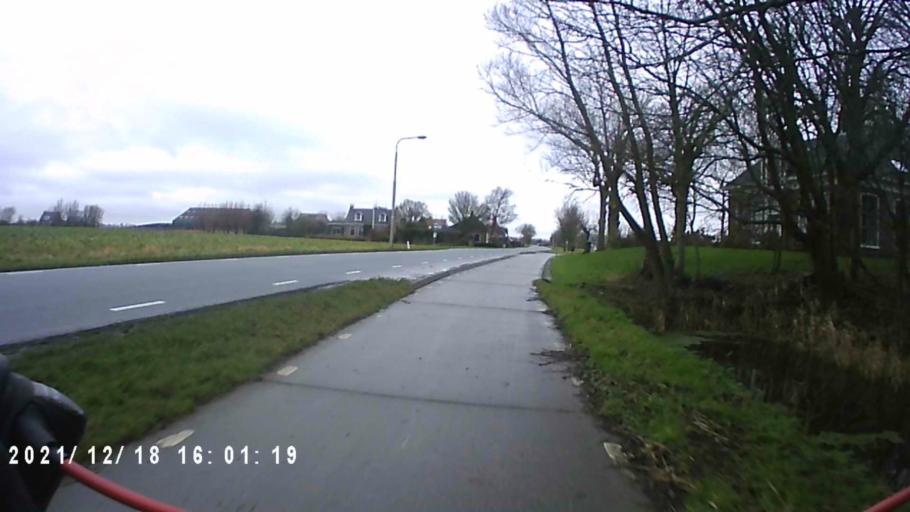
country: NL
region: Friesland
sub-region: Gemeente Dongeradeel
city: Anjum
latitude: 53.3444
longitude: 6.0860
